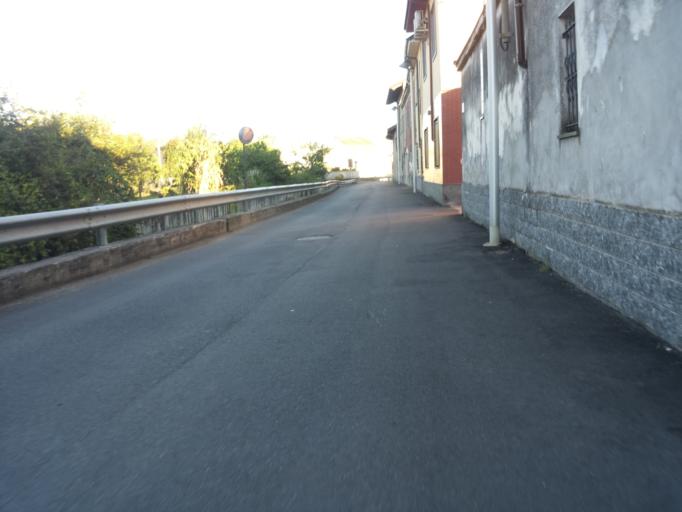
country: IT
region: Piedmont
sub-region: Provincia di Vercelli
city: Pezzana
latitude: 45.2615
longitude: 8.4909
